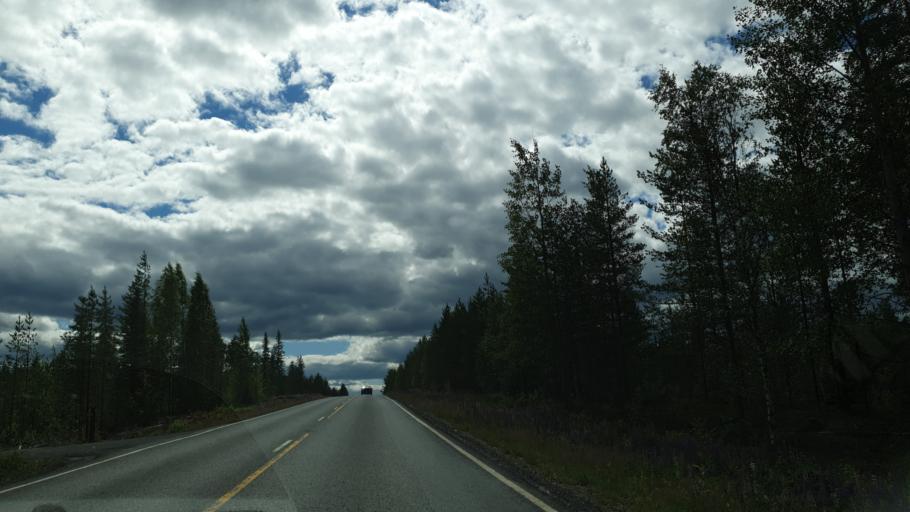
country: FI
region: Kainuu
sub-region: Kehys-Kainuu
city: Kuhmo
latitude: 64.0863
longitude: 29.4831
